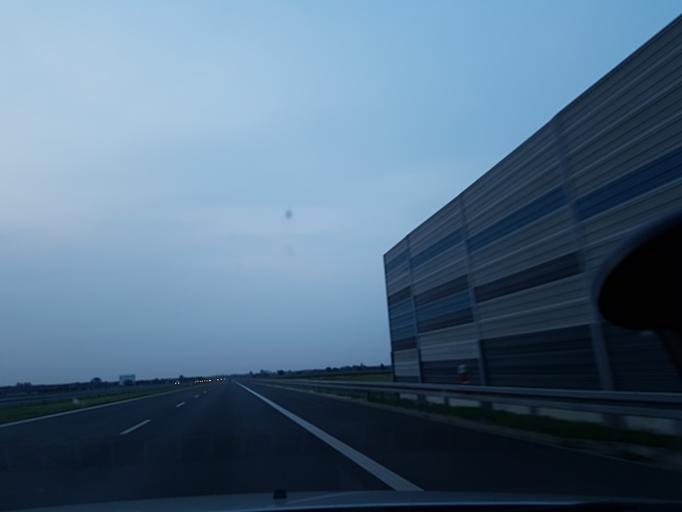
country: PL
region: Lodz Voivodeship
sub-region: Powiat zgierski
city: Strykow
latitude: 51.9728
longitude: 19.5727
